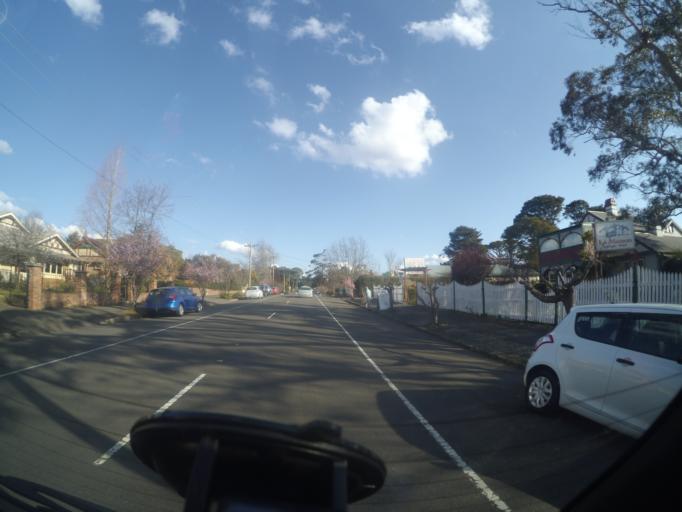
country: AU
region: New South Wales
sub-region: Blue Mountains Municipality
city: Katoomba
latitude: -33.7255
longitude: 150.3108
